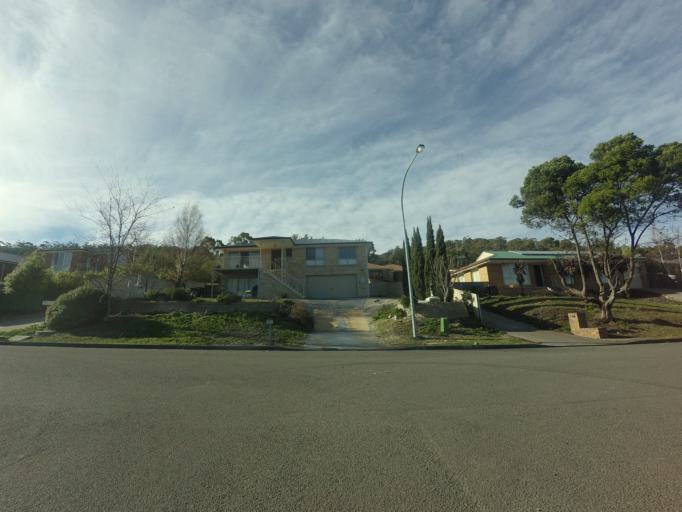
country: AU
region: Tasmania
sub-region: Clarence
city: Rokeby
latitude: -42.9004
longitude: 147.4598
